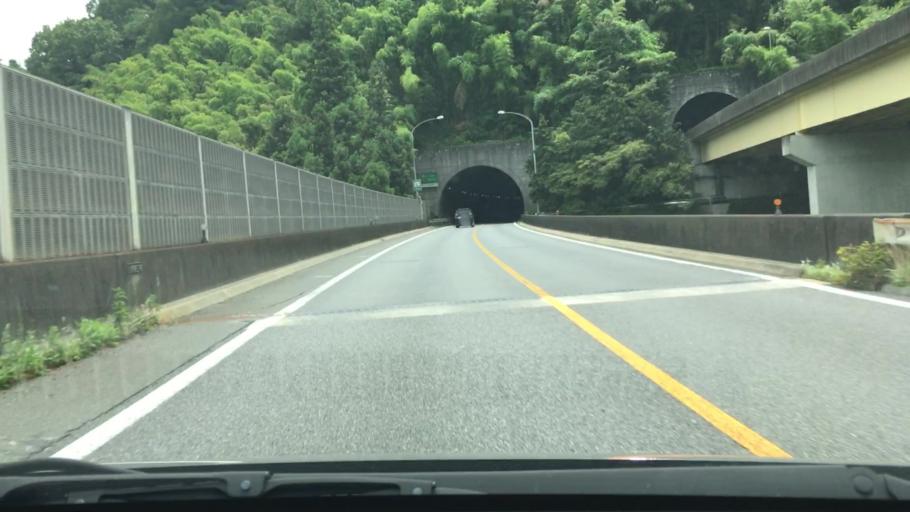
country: JP
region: Yamaguchi
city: Otake
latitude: 34.2191
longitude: 132.1981
